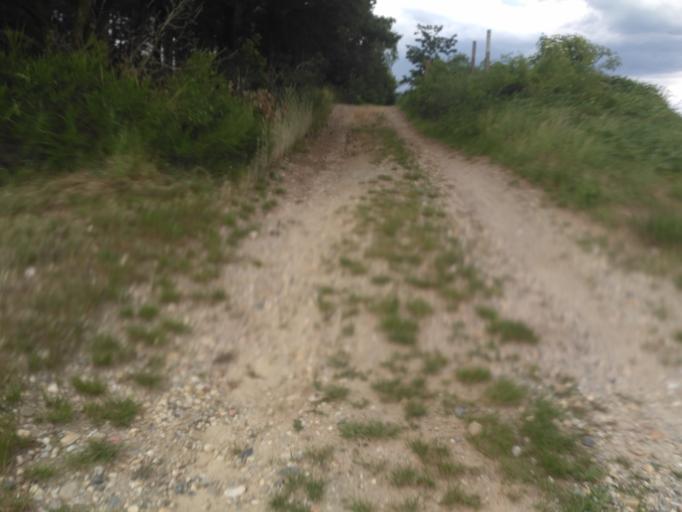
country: DE
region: Brandenburg
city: Hohenleipisch
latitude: 51.4954
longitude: 13.5250
